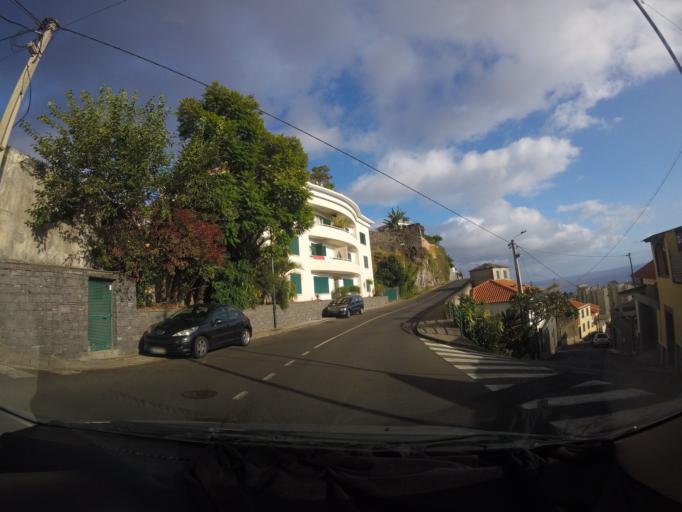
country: PT
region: Madeira
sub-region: Funchal
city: Nossa Senhora do Monte
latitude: 32.6594
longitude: -16.9124
